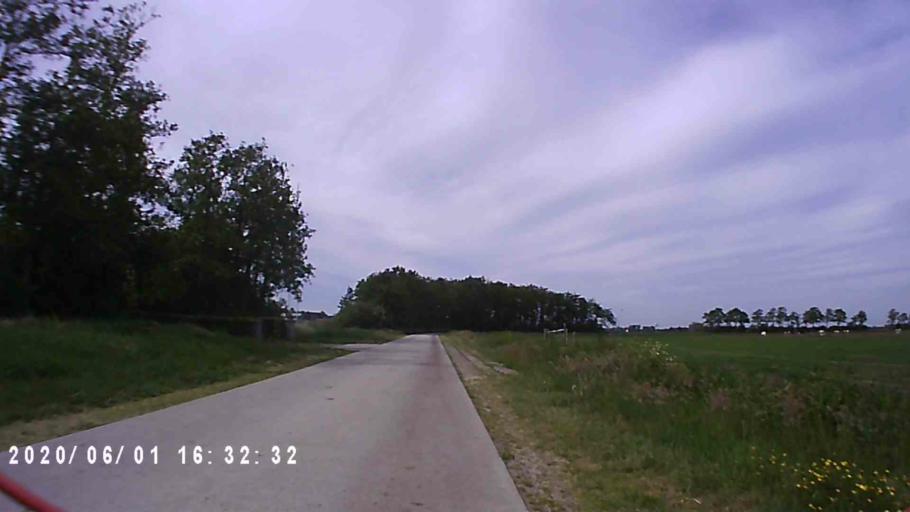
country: NL
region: Friesland
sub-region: Gemeente Leeuwarden
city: Camminghaburen
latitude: 53.1899
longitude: 5.8644
